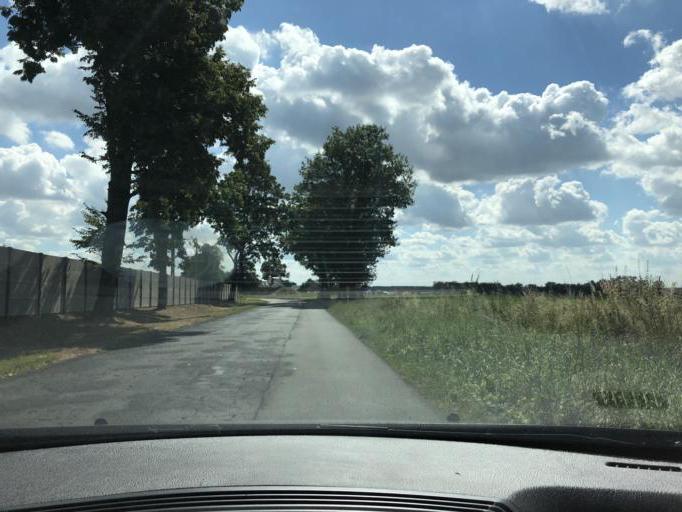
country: PL
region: Lodz Voivodeship
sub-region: Powiat wieruszowski
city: Czastary
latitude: 51.2389
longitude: 18.3380
